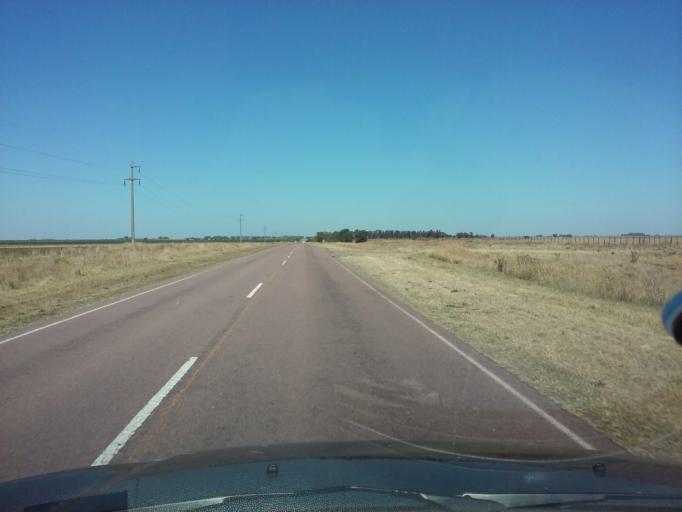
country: AR
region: La Pampa
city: Colonia Baron
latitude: -36.2539
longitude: -63.9428
